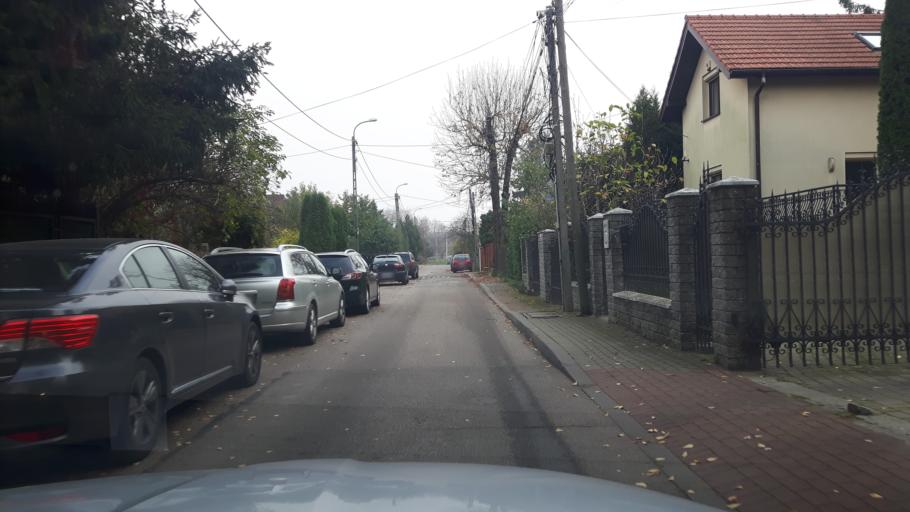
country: PL
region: Masovian Voivodeship
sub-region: Warszawa
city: Wlochy
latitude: 52.1967
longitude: 20.9348
